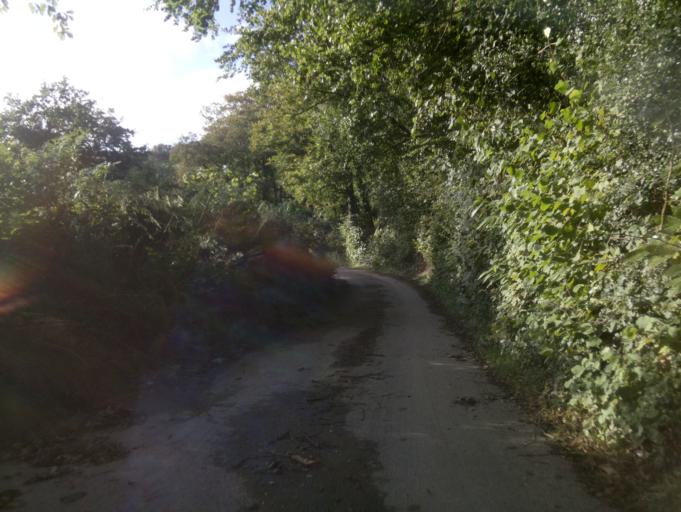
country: GB
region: England
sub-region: Devon
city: Totnes
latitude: 50.3459
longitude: -3.6682
